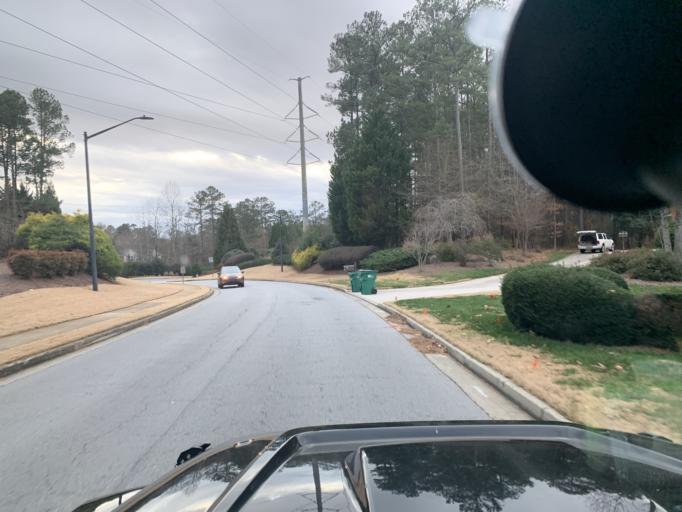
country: US
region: Georgia
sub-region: Cherokee County
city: Woodstock
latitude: 34.0995
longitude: -84.4678
